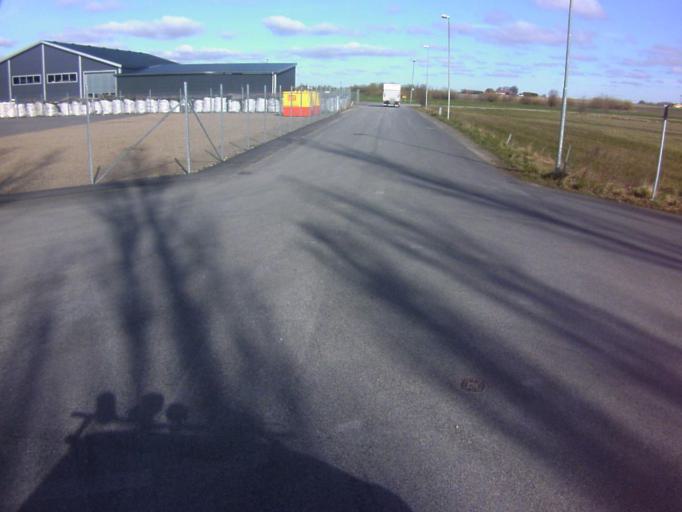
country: SE
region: Skane
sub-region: Kavlinge Kommun
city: Kaevlinge
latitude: 55.7998
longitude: 13.1228
